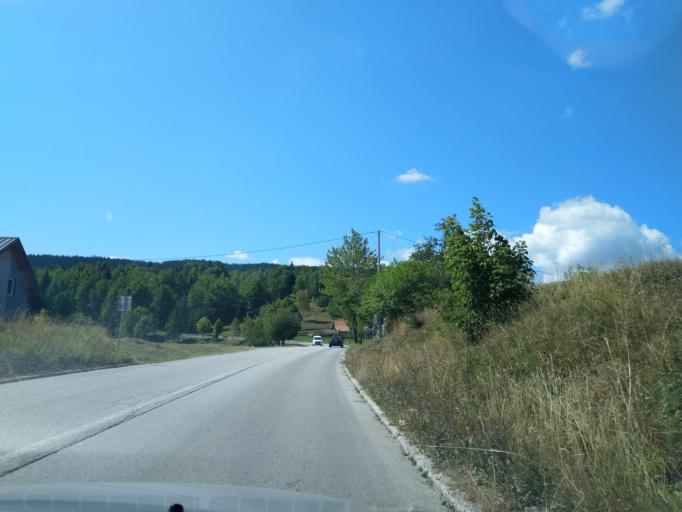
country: RS
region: Central Serbia
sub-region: Zlatiborski Okrug
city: Nova Varos
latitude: 43.4204
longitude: 19.8289
